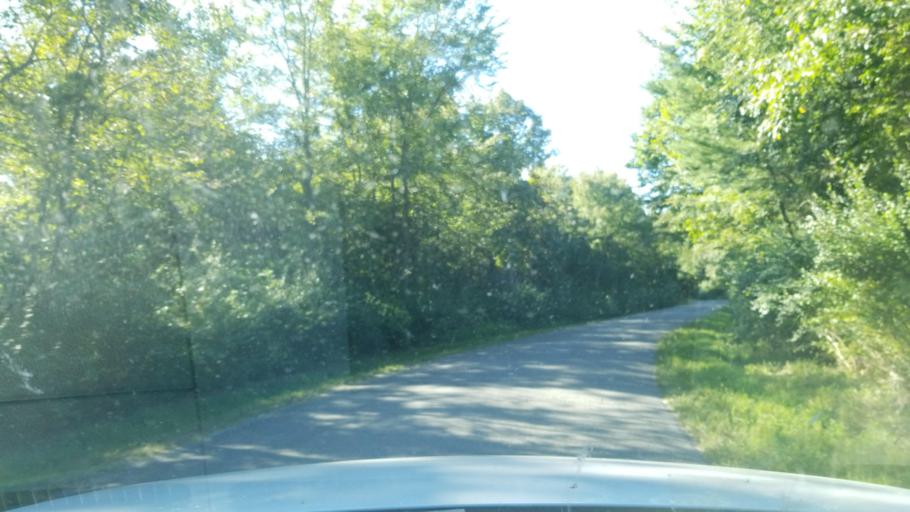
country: US
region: Illinois
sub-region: Hardin County
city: Elizabethtown
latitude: 37.5997
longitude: -88.3724
